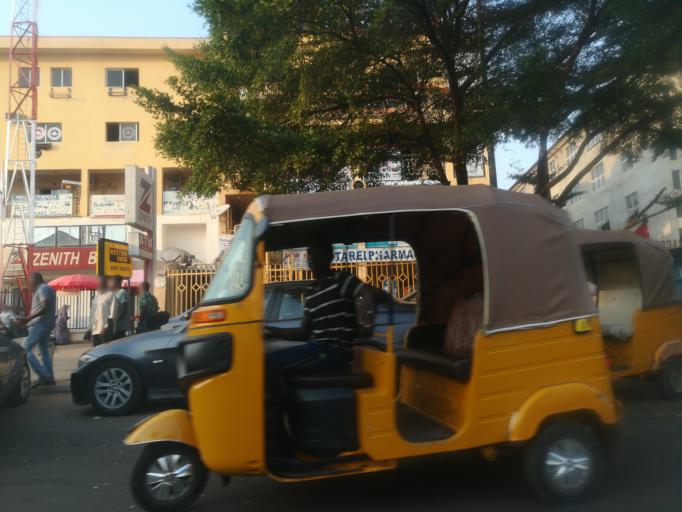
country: NG
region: Abuja Federal Capital Territory
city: Abuja
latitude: 9.0670
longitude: 7.4449
